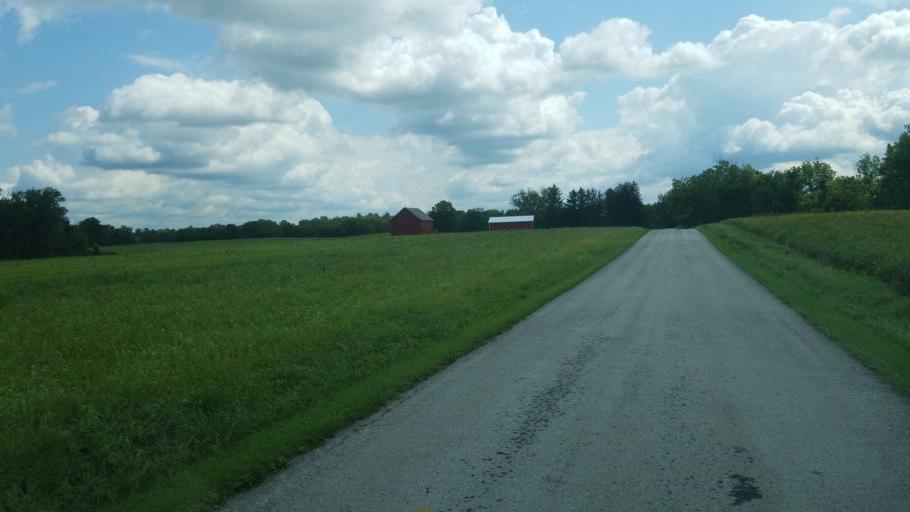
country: US
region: Ohio
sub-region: Huron County
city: Monroeville
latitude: 41.1680
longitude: -82.7175
